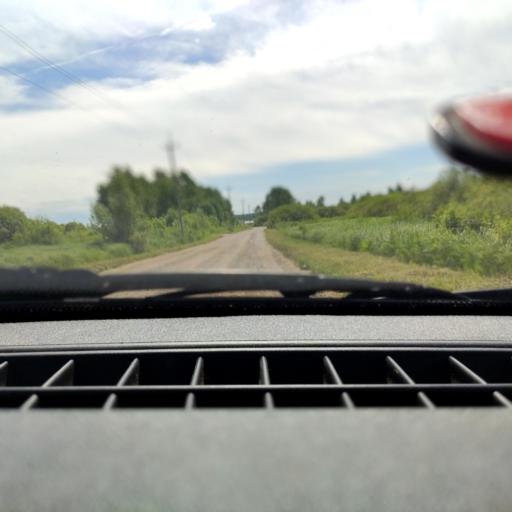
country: RU
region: Bashkortostan
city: Kabakovo
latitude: 54.7290
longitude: 56.2027
